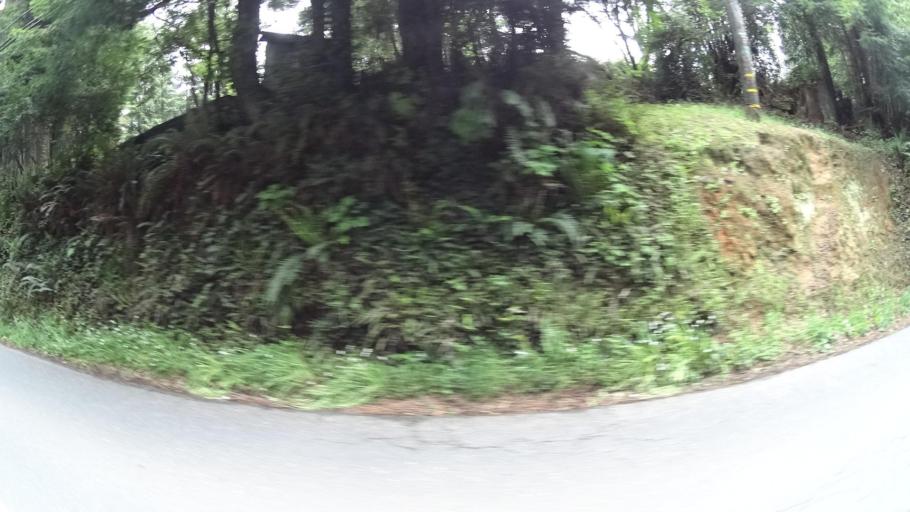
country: US
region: California
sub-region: Humboldt County
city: Bayside
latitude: 40.7935
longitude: -124.0561
